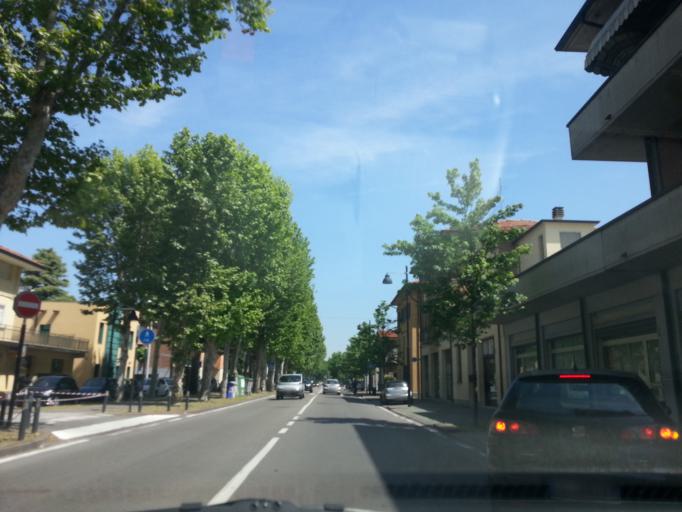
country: IT
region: Emilia-Romagna
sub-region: Provincia di Reggio Emilia
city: Scandiano
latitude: 44.6013
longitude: 10.6865
